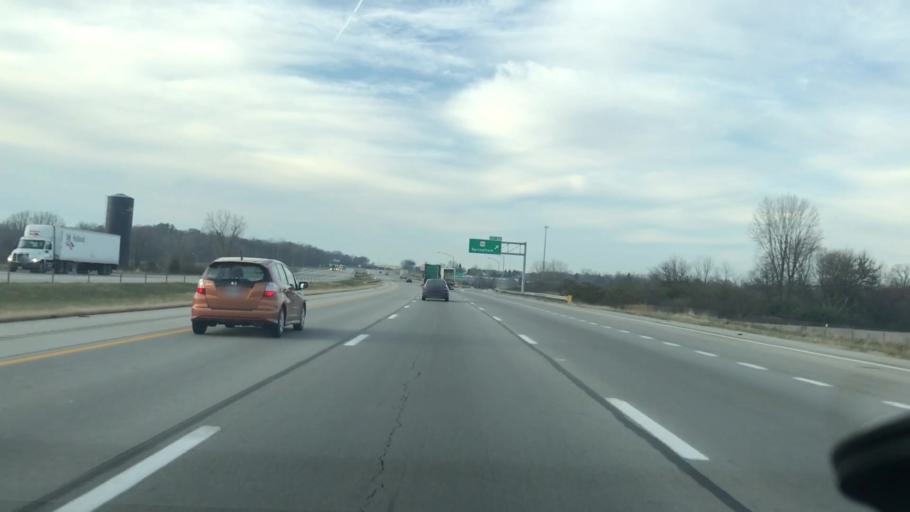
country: US
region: Ohio
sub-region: Clark County
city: Lisbon
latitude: 39.9276
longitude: -83.6843
